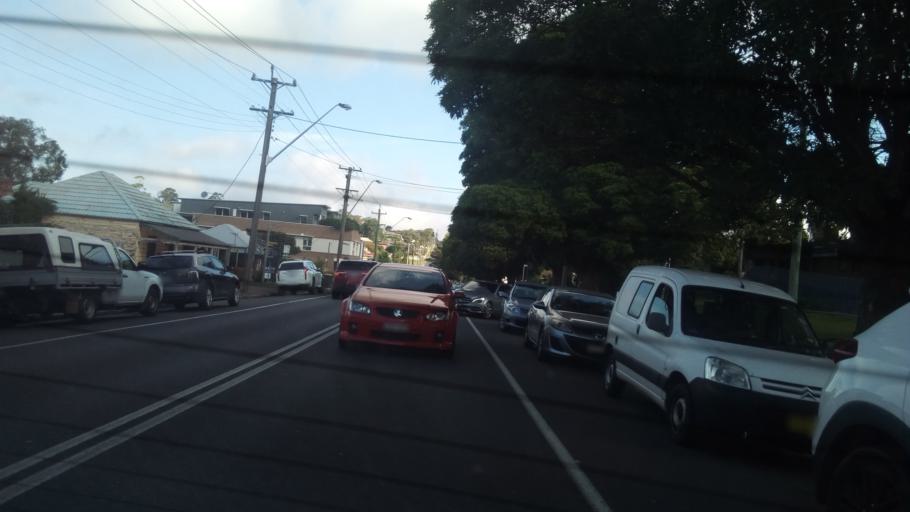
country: AU
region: New South Wales
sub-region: Wollongong
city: Helensburgh
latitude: -34.1925
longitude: 150.9817
